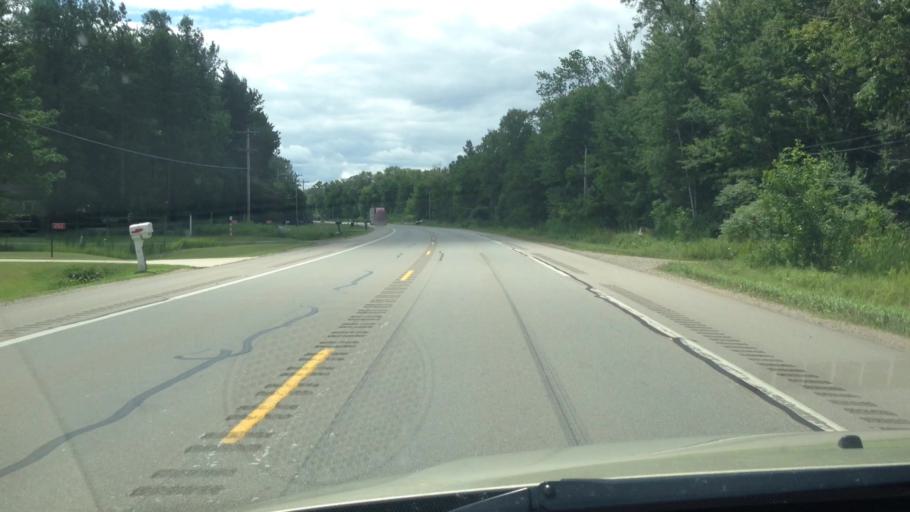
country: US
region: Michigan
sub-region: Menominee County
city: Menominee
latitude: 45.1691
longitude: -87.5841
